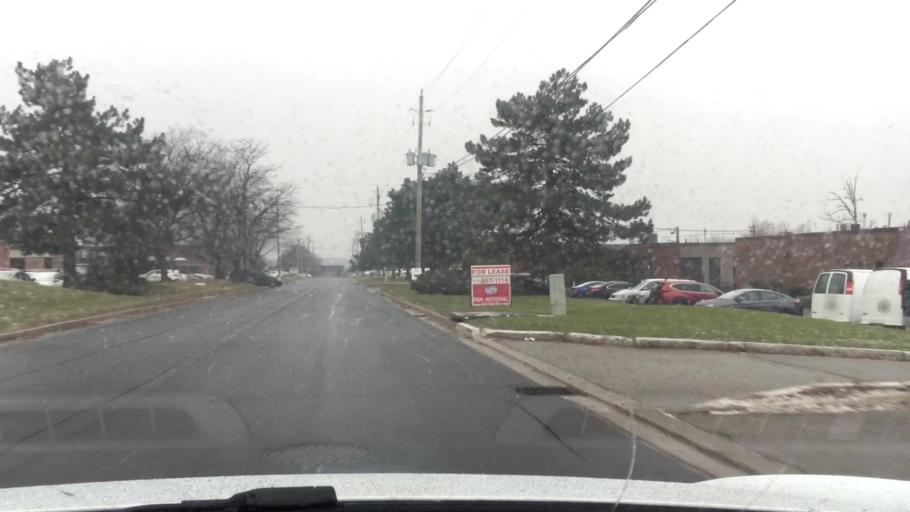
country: CA
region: Ontario
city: Willowdale
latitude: 43.8252
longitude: -79.3445
